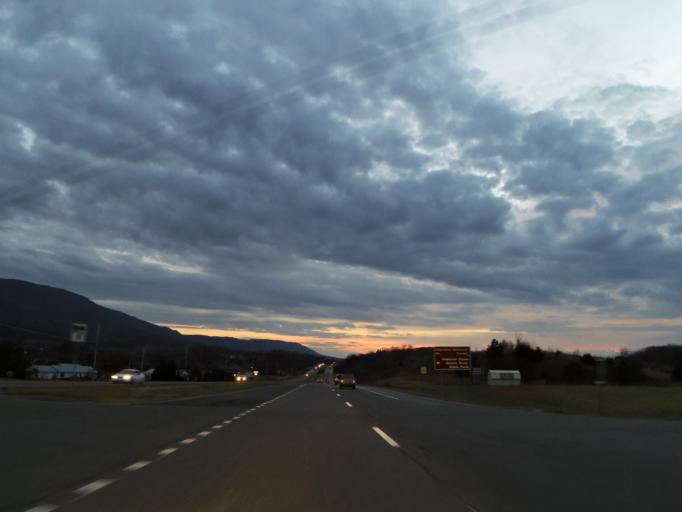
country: US
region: Tennessee
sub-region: McMinn County
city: Etowah
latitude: 35.2465
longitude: -84.5596
